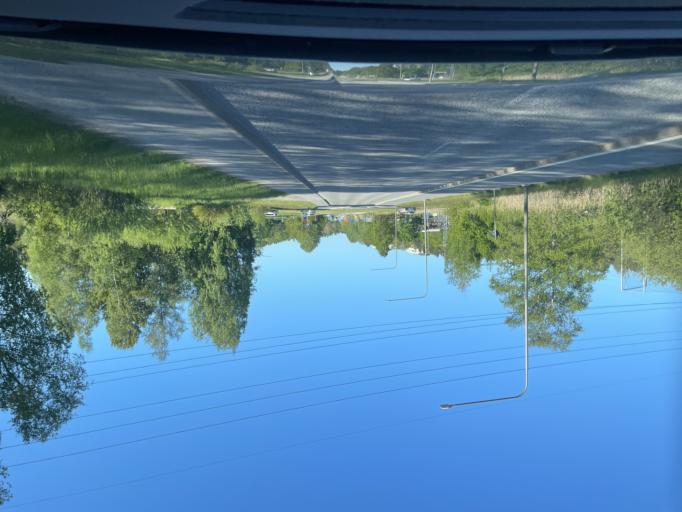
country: SE
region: Stockholm
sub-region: Haninge Kommun
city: Handen
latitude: 59.2193
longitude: 18.1398
